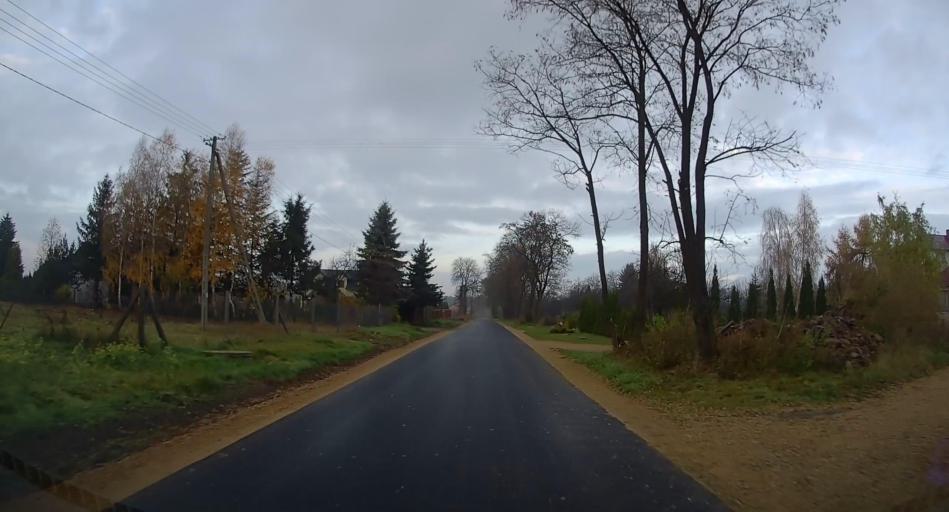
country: PL
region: Lodz Voivodeship
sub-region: Powiat skierniewicki
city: Kowiesy
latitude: 51.9259
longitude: 20.4058
